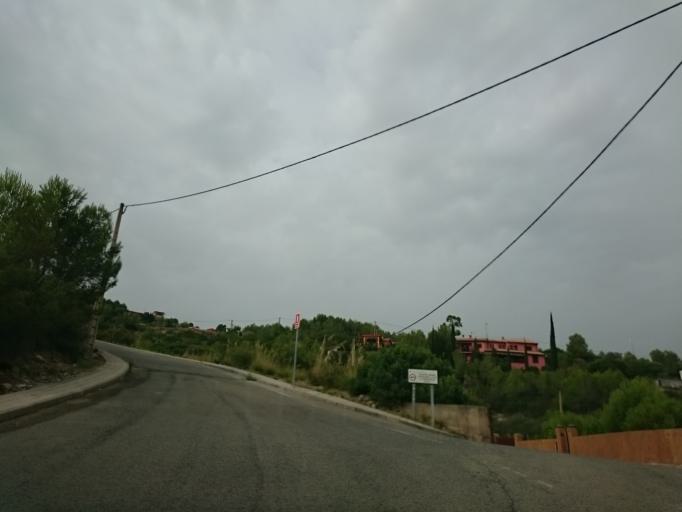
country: ES
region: Catalonia
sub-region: Provincia de Barcelona
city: Olivella
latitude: 41.2931
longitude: 1.8591
